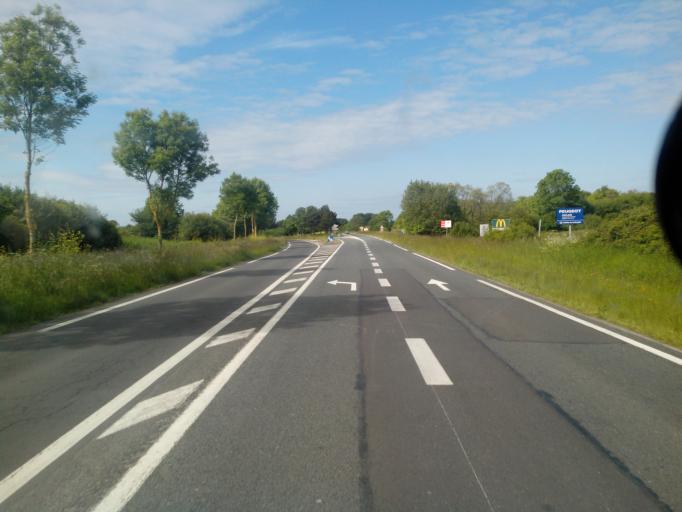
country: FR
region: Lower Normandy
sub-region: Departement du Calvados
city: Dives-sur-Mer
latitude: 49.2685
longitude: -0.1037
